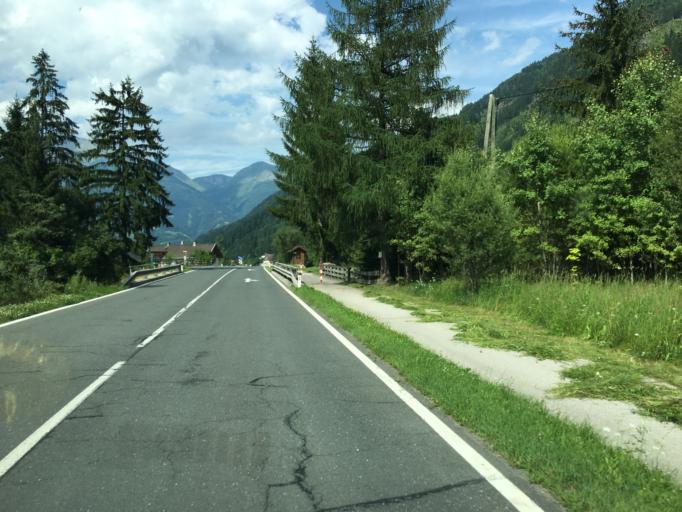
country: AT
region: Carinthia
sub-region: Politischer Bezirk Spittal an der Drau
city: Stall
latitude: 46.8971
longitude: 13.0635
